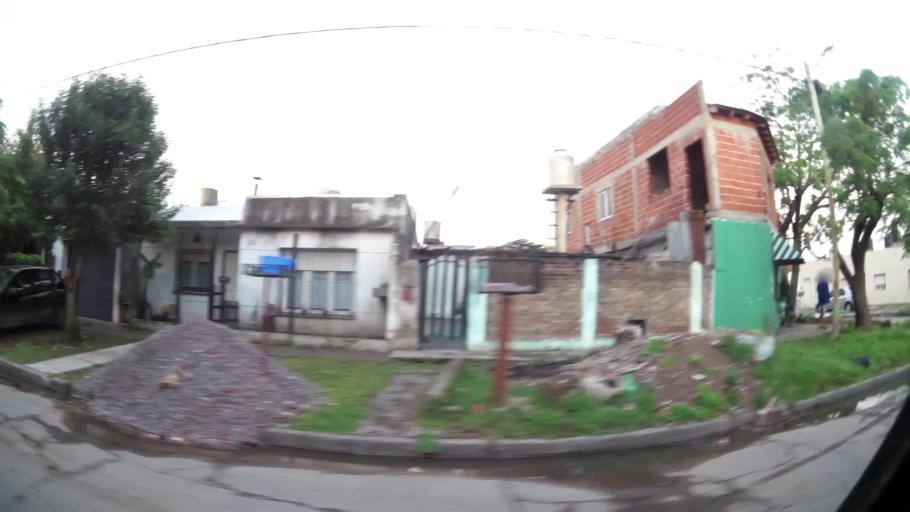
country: AR
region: Buenos Aires
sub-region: Partido de Lomas de Zamora
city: Lomas de Zamora
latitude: -34.7601
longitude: -58.3735
